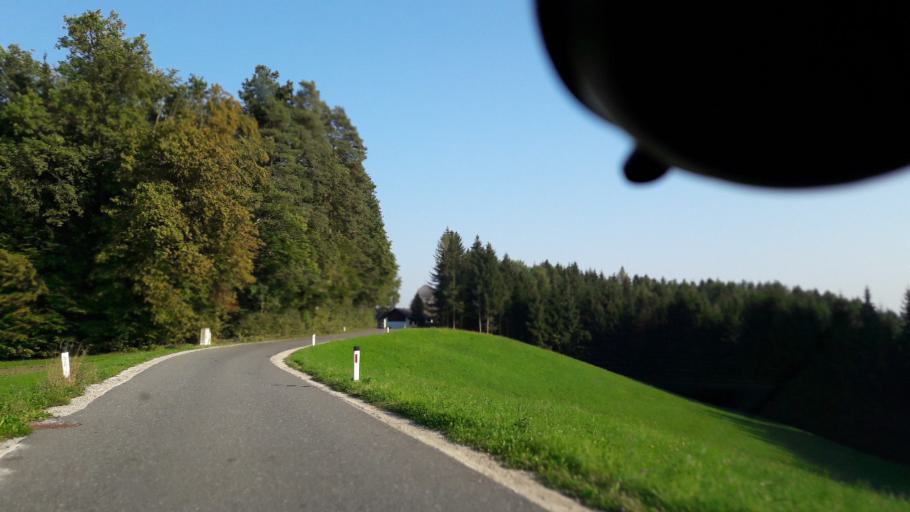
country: AT
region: Styria
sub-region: Politischer Bezirk Graz-Umgebung
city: Sankt Oswald bei Plankenwarth
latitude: 47.0934
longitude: 15.2540
